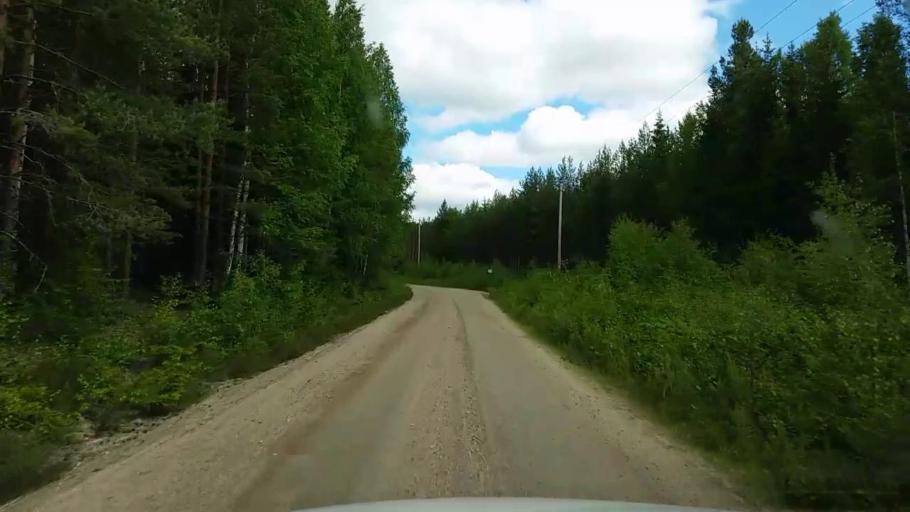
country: SE
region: Gaevleborg
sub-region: Ovanakers Kommun
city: Edsbyn
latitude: 61.5267
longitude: 15.9378
